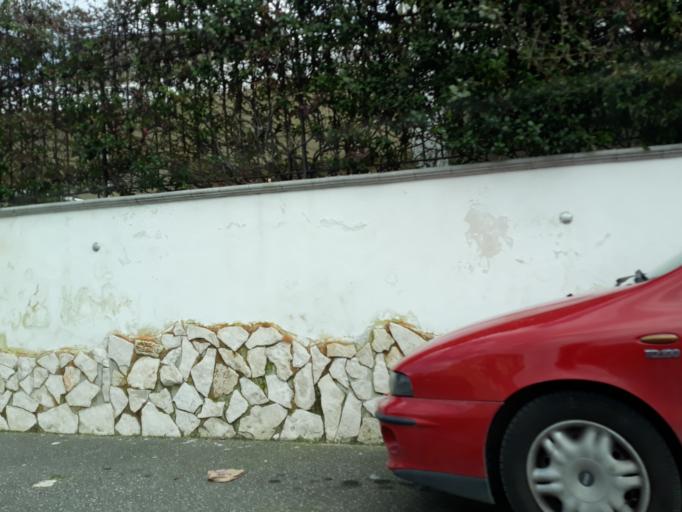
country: IT
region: Campania
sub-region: Provincia di Napoli
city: Melito di Napoli
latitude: 40.8889
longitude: 14.2330
